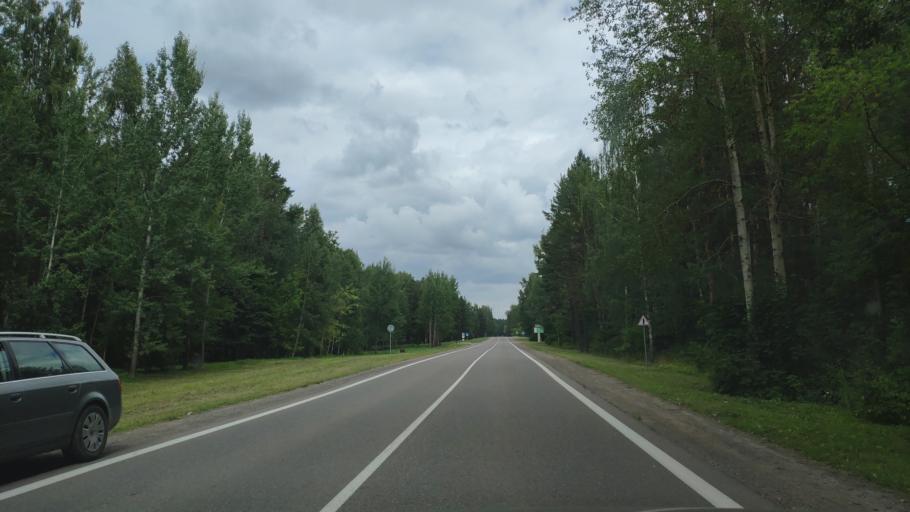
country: BY
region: Minsk
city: Zhdanovichy
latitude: 53.9703
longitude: 27.4325
